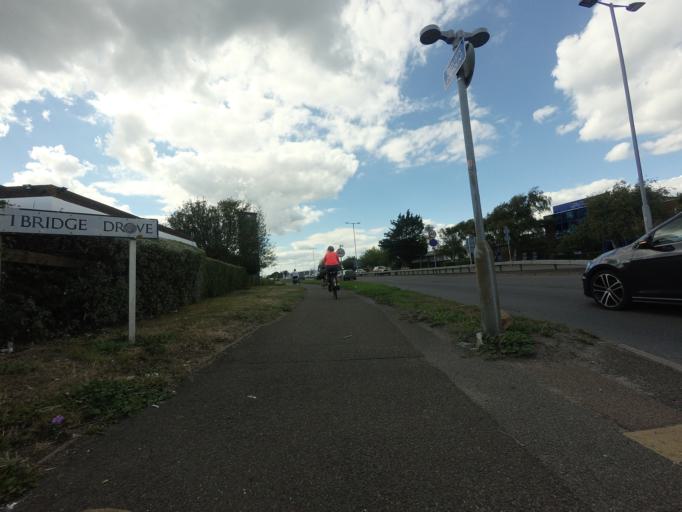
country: GB
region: England
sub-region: East Sussex
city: Eastbourne
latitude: 50.7873
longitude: 0.3039
